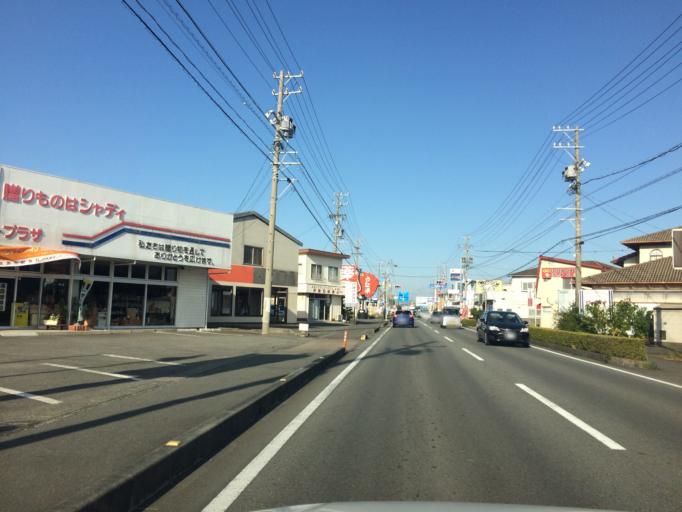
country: JP
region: Shizuoka
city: Shimada
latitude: 34.7642
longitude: 138.2480
